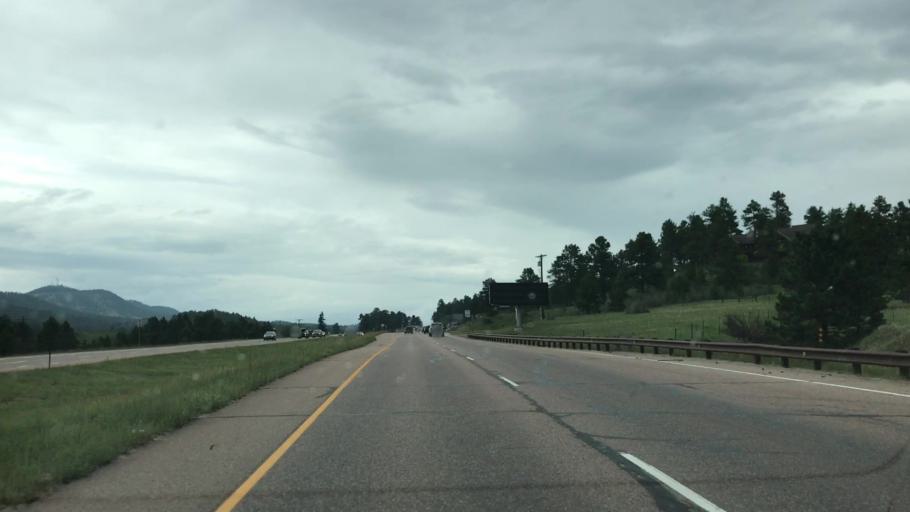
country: US
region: Colorado
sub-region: El Paso County
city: Cascade-Chipita Park
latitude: 38.9647
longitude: -105.0316
